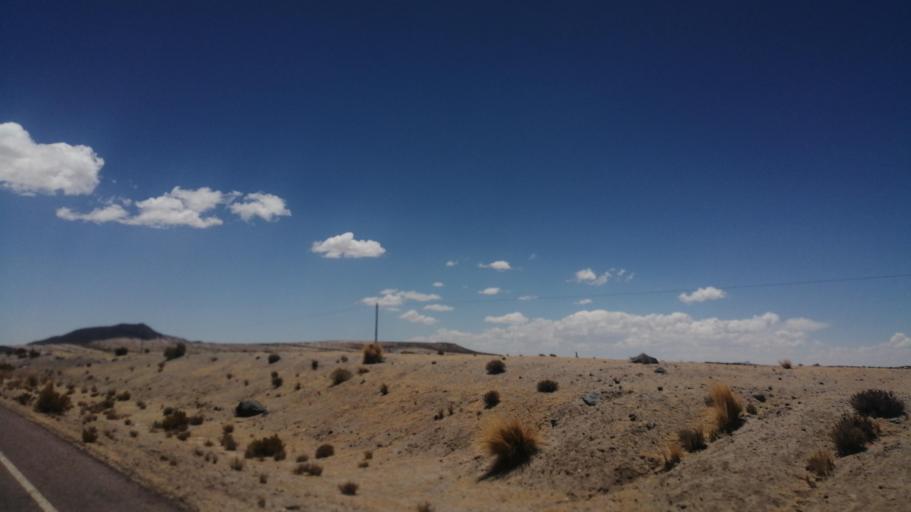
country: BO
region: Oruro
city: Challapata
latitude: -19.2192
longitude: -66.9975
